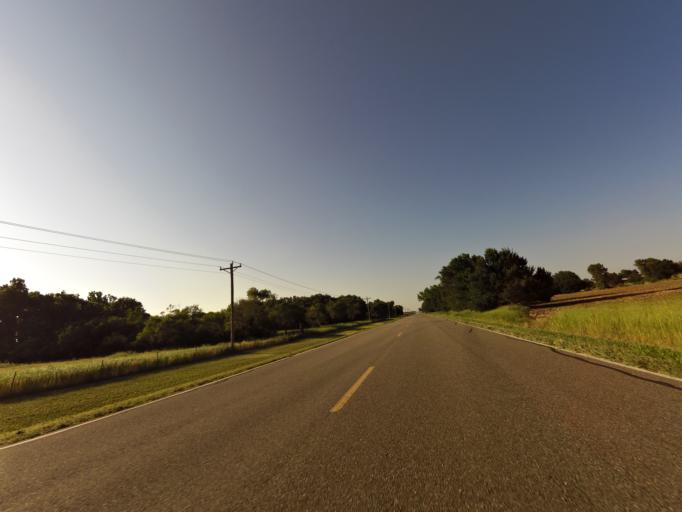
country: US
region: Kansas
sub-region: Reno County
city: Buhler
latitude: 38.1684
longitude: -97.8487
